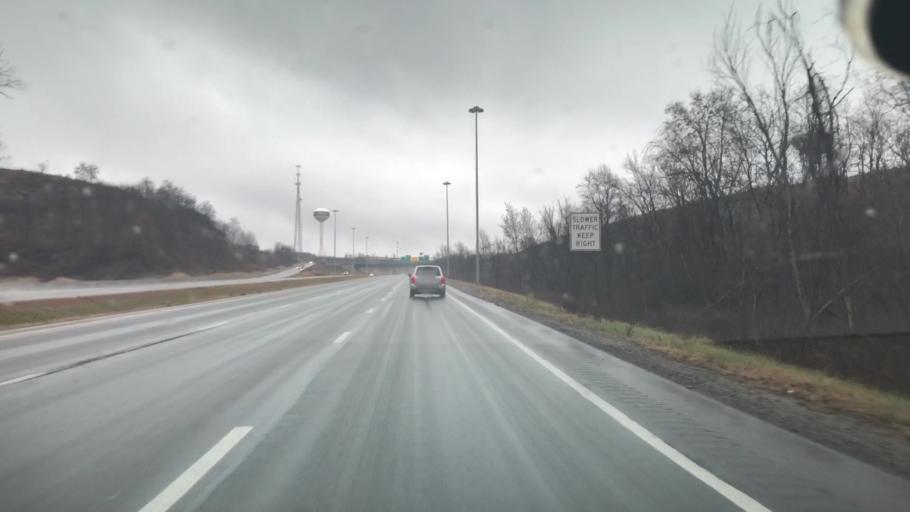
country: US
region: West Virginia
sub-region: Ohio County
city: Bethlehem
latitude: 40.0557
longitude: -80.5956
